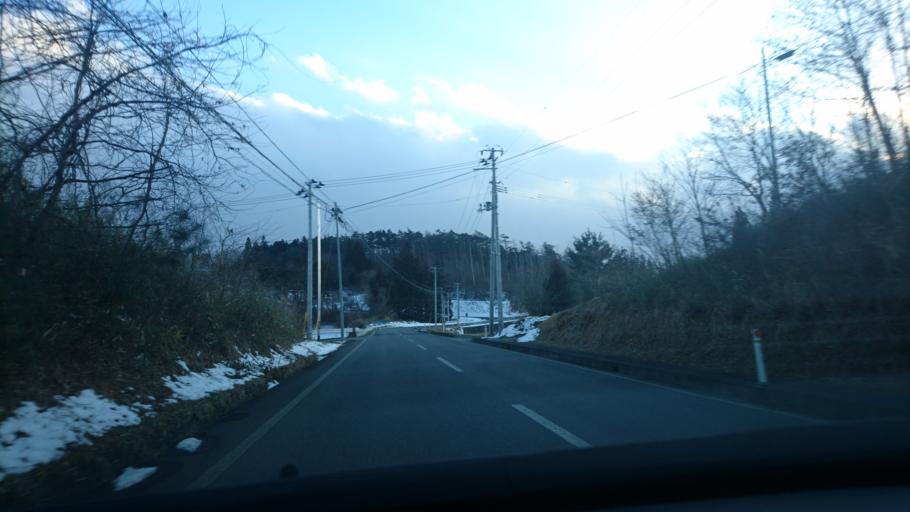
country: JP
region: Iwate
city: Ichinoseki
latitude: 39.0102
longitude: 141.3368
